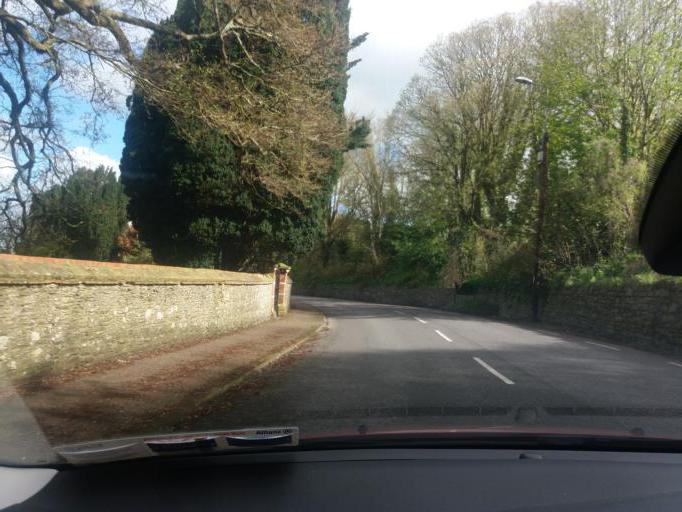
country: IE
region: Munster
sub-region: County Cork
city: Passage West
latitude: 51.8568
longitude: -8.3256
